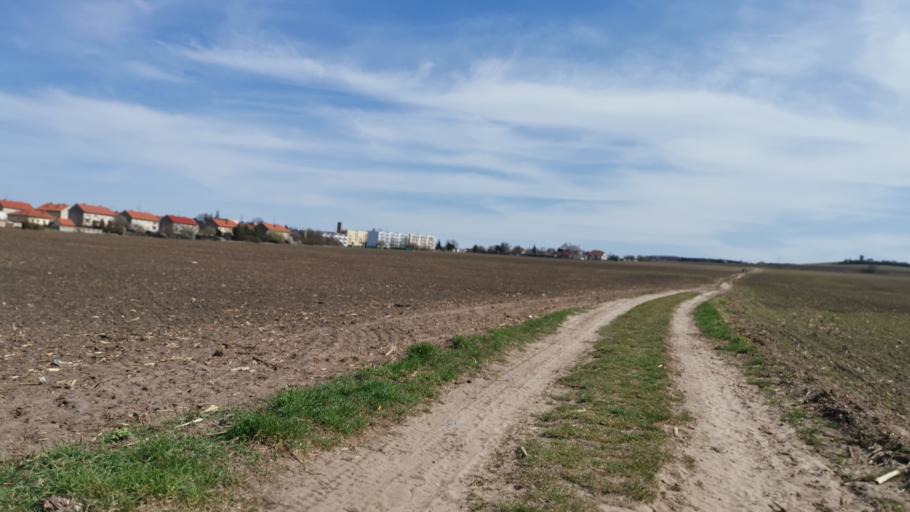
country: SK
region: Trnavsky
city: Gbely
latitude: 48.7142
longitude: 17.1117
